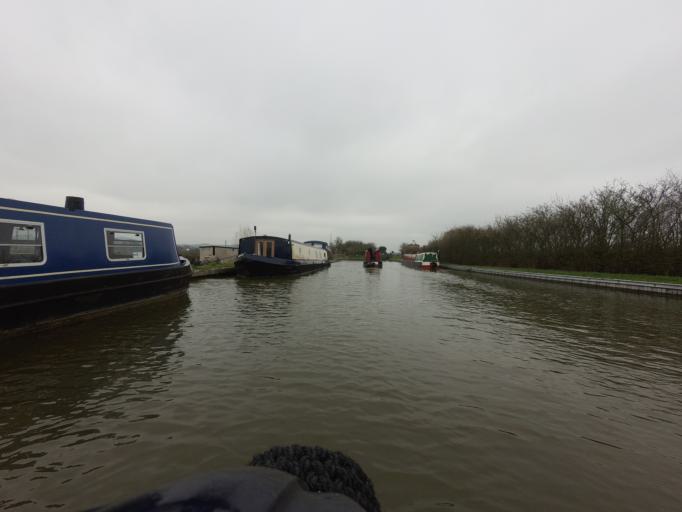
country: GB
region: England
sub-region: Buckinghamshire
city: Ivinghoe
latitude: 51.8472
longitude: -0.6441
